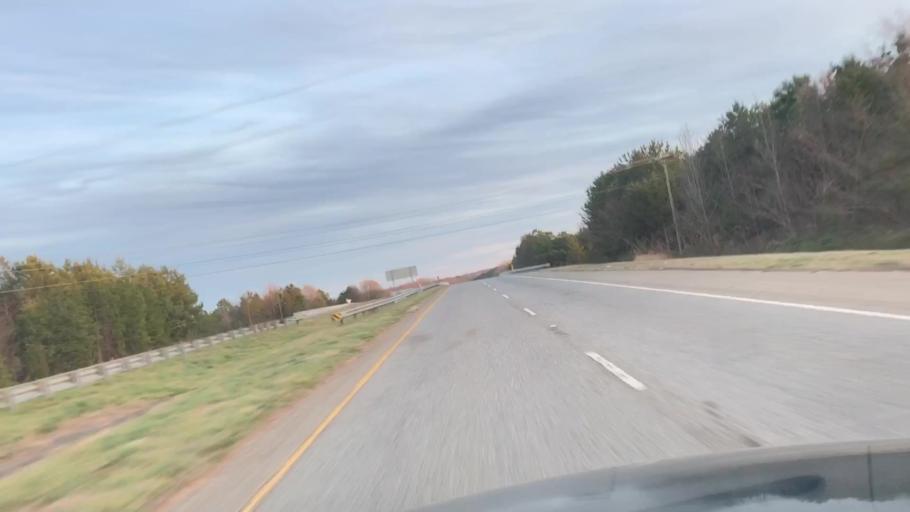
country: US
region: South Carolina
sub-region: Greenville County
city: Golden Grove
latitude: 34.7427
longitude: -82.4374
